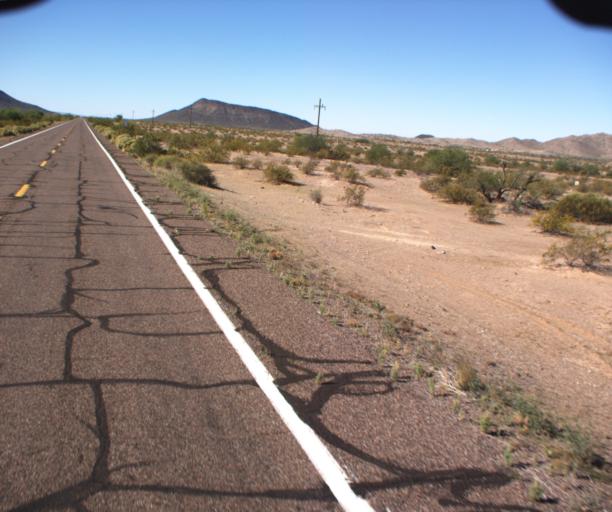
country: US
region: Arizona
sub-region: Maricopa County
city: Gila Bend
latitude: 32.7946
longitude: -112.8026
